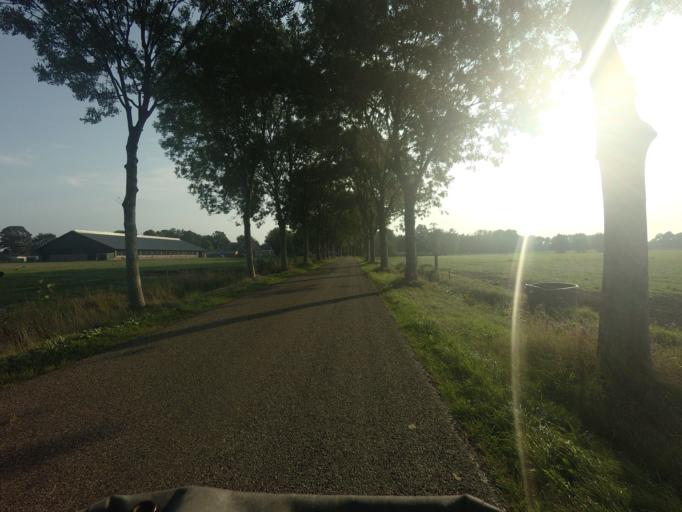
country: NL
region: Drenthe
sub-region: Gemeente Tynaarlo
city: Vries
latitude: 53.1155
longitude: 6.5260
